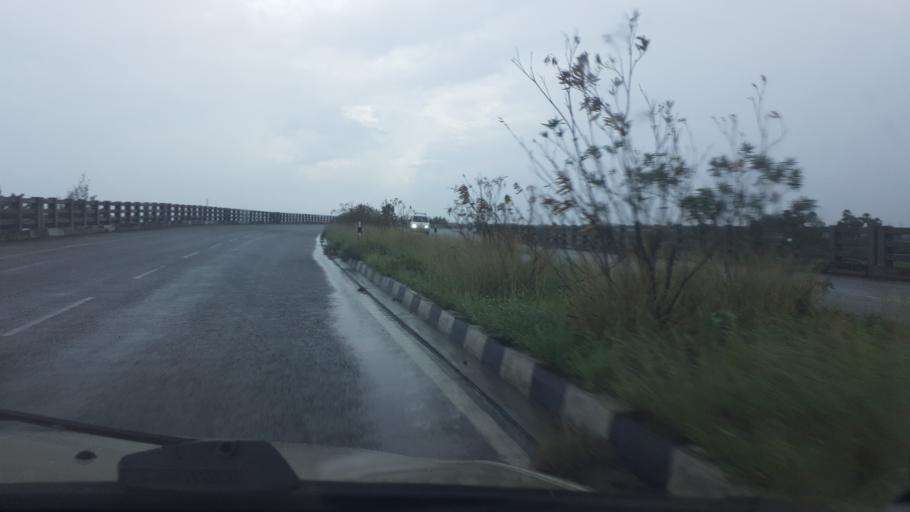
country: IN
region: Tamil Nadu
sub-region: Thoothukkudi
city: Kayattar
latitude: 8.9612
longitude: 77.7729
